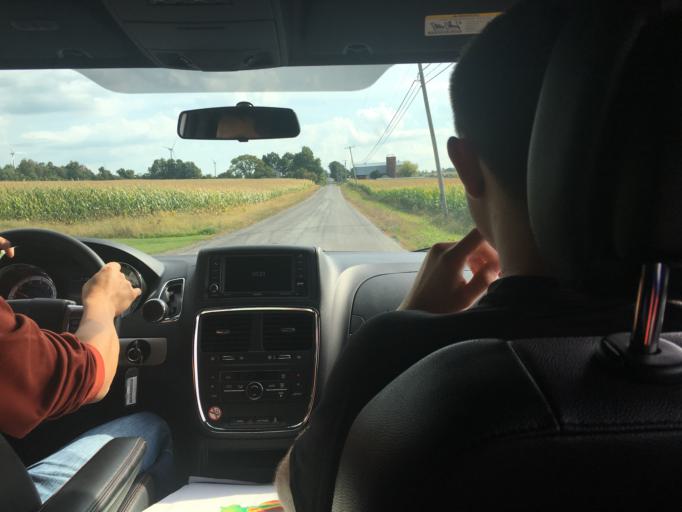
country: US
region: New York
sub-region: Madison County
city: Cazenovia
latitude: 42.9819
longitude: -75.7827
